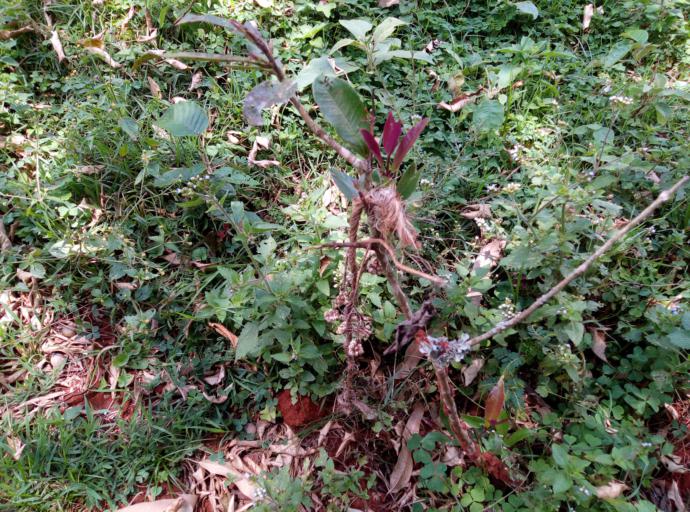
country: KE
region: Kirinyaga
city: Keruguya
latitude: -0.4751
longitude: 37.1405
